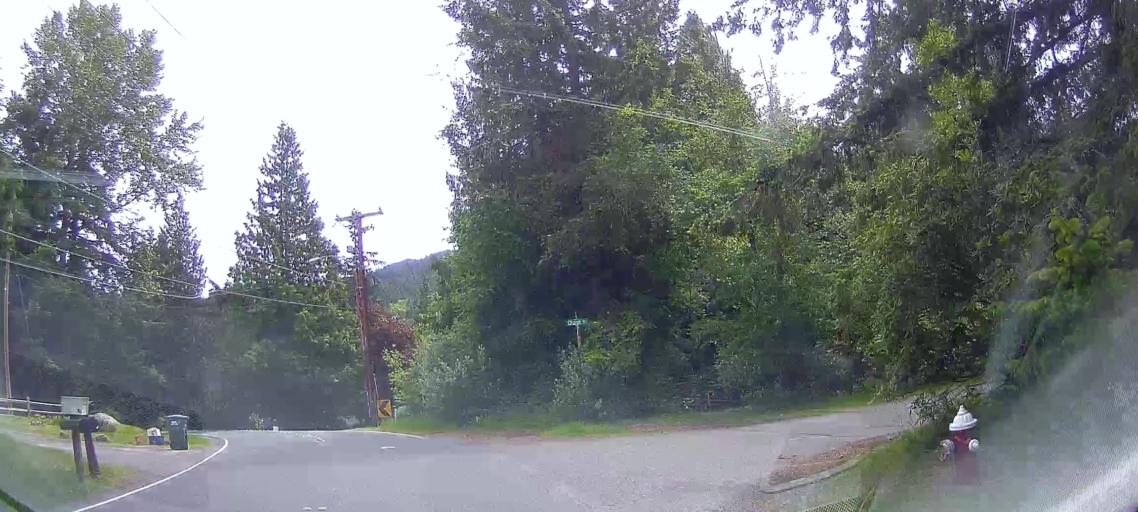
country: US
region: Washington
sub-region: Whatcom County
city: Bellingham
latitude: 48.7039
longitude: -122.4783
